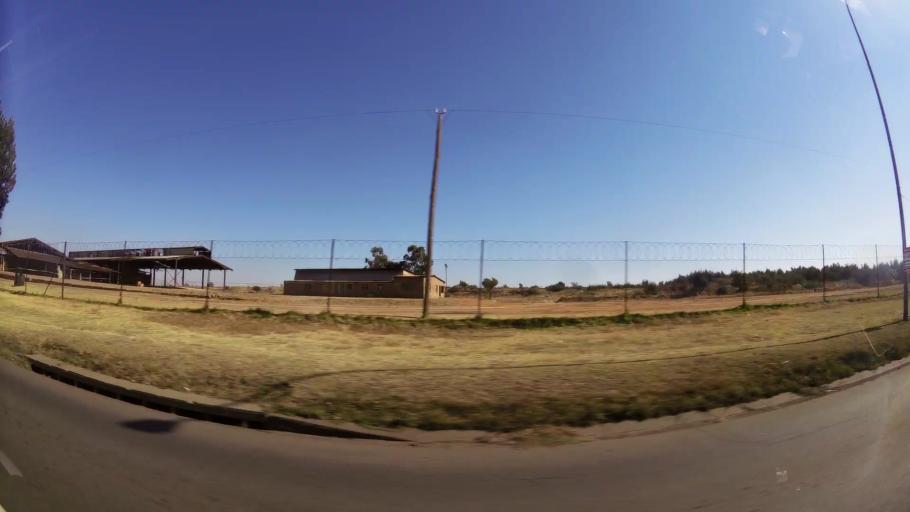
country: ZA
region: Mpumalanga
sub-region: Nkangala District Municipality
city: Witbank
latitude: -25.8508
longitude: 29.2343
